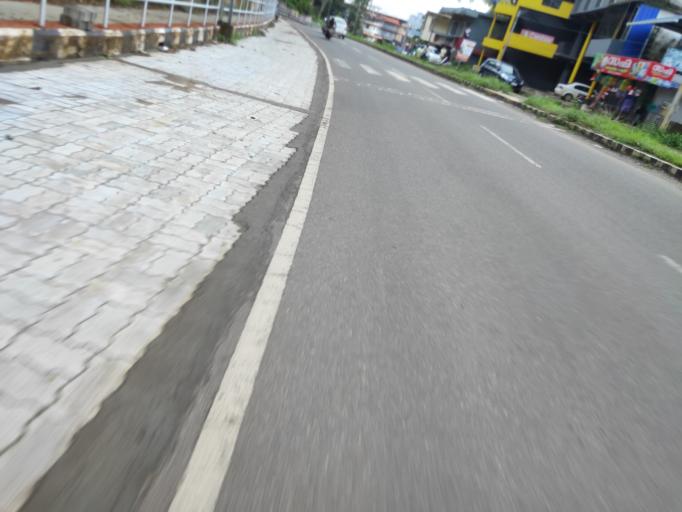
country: IN
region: Kerala
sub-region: Malappuram
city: Manjeri
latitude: 11.1968
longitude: 76.2282
